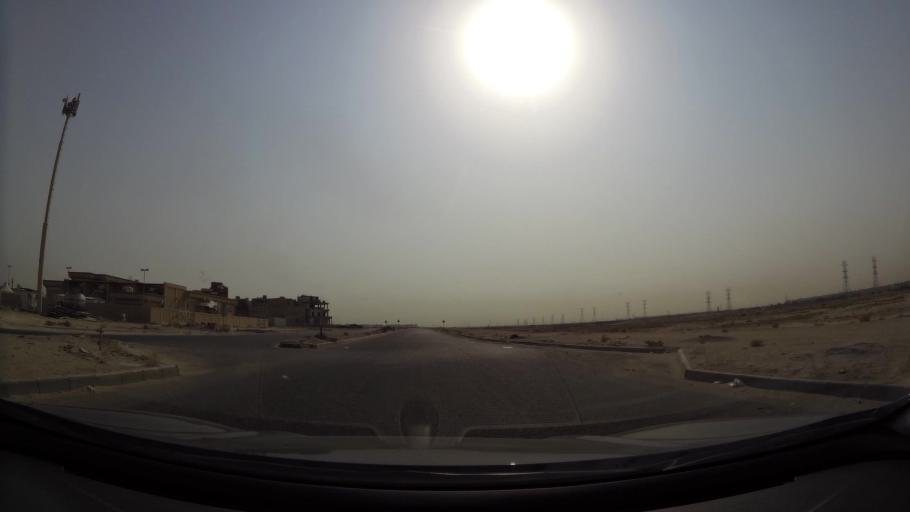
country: KW
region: Muhafazat al Jahra'
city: Al Jahra'
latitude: 29.3422
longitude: 47.7392
